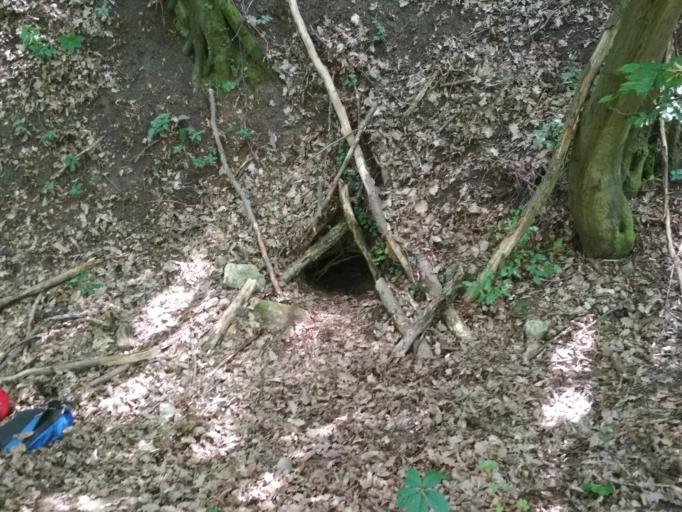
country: HU
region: Komarom-Esztergom
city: Esztergom
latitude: 47.8257
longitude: 18.7774
